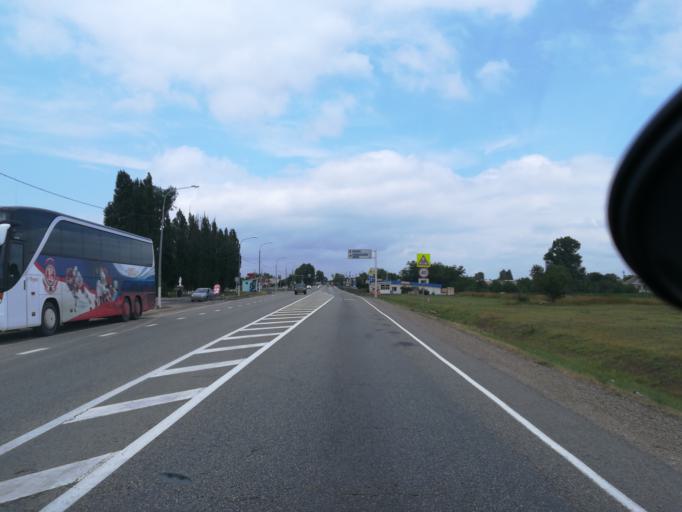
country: RU
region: Krasnodarskiy
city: Korzhevskiy
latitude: 45.1977
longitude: 37.6656
